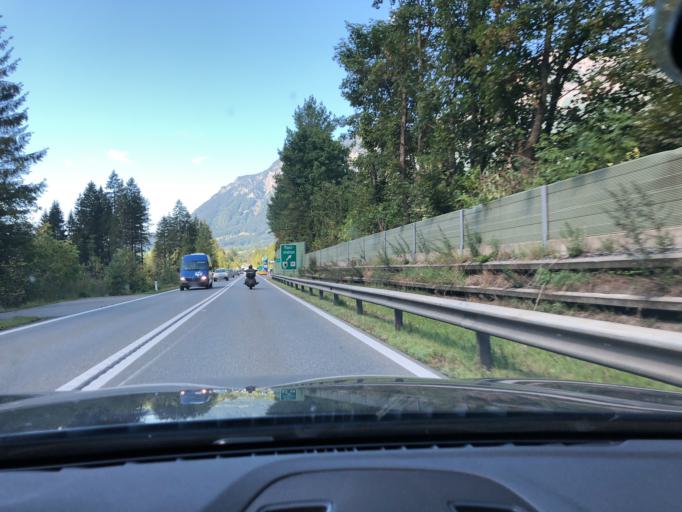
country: AT
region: Vorarlberg
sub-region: Politischer Bezirk Bludenz
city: Innerbraz
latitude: 47.1394
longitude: 9.9283
